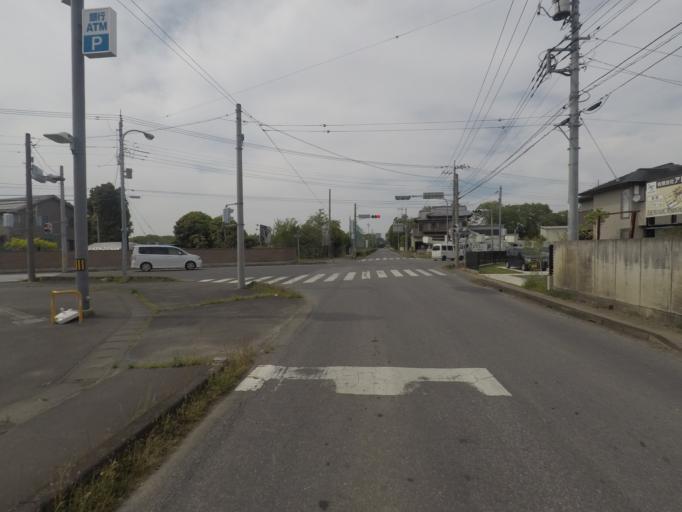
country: JP
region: Ibaraki
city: Shimodate
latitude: 36.2449
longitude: 140.0293
